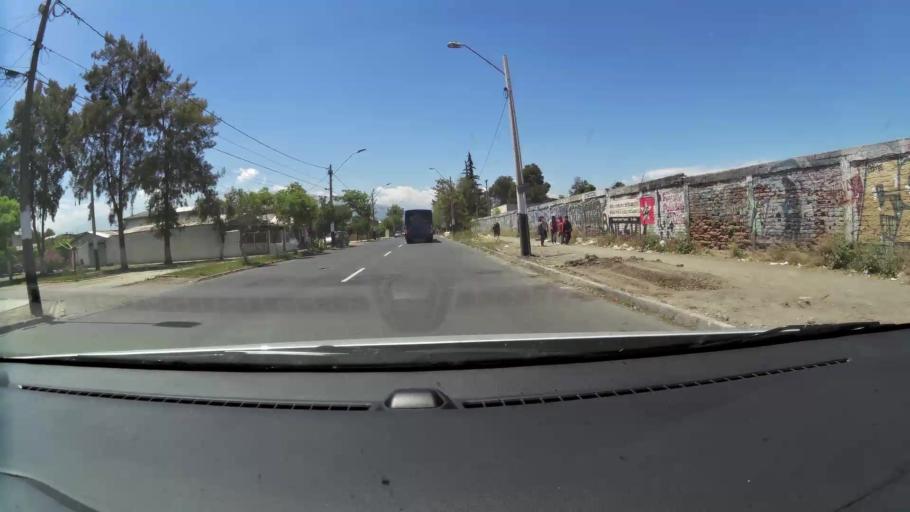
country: CL
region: Santiago Metropolitan
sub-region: Provincia de Santiago
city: La Pintana
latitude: -33.5558
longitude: -70.6491
